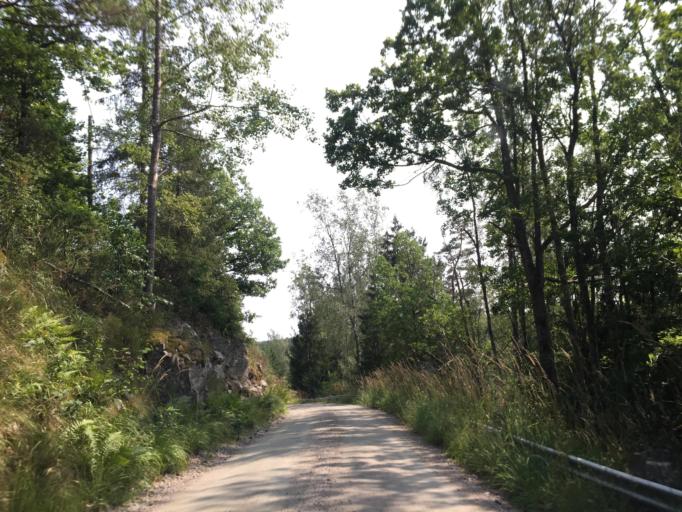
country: SE
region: Vaestra Goetaland
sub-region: Lilla Edets Kommun
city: Lilla Edet
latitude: 58.2404
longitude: 12.0772
